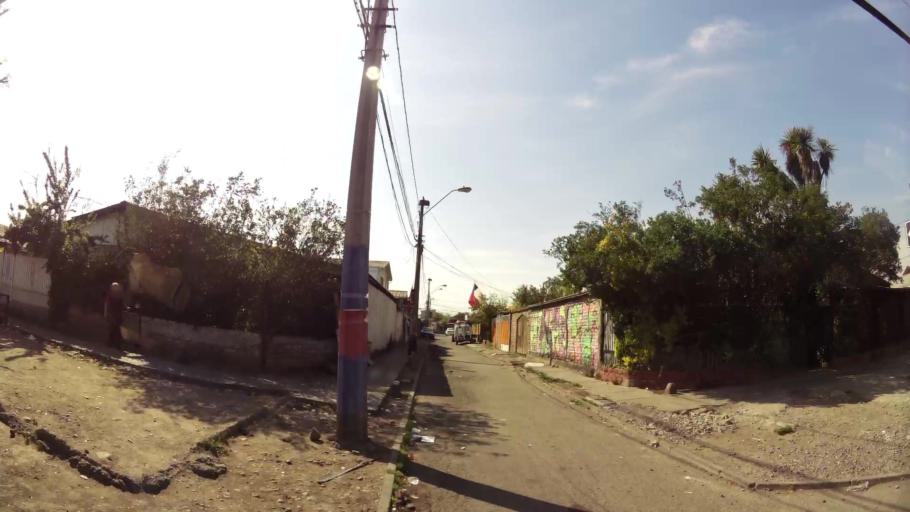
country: CL
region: Santiago Metropolitan
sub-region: Provincia de Santiago
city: La Pintana
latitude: -33.5575
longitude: -70.6616
